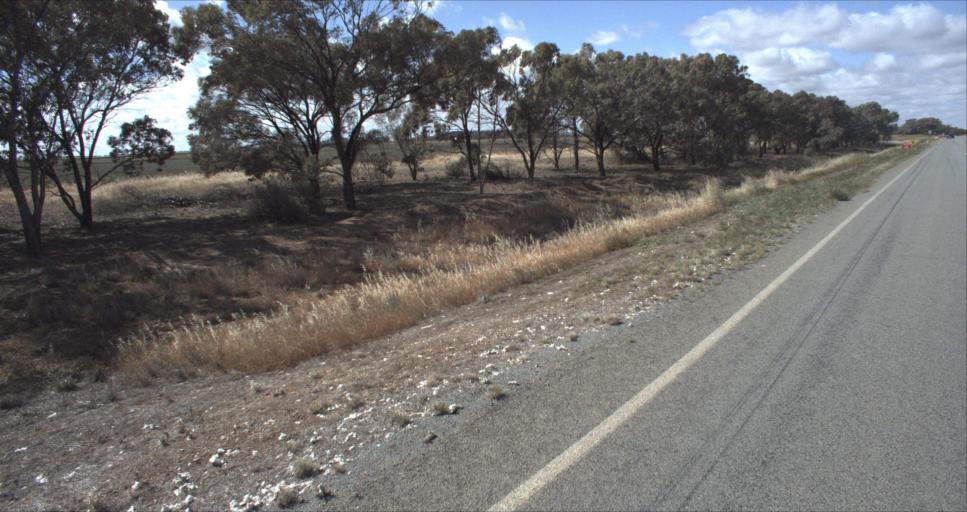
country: AU
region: New South Wales
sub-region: Murrumbidgee Shire
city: Darlington Point
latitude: -34.5501
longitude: 146.1708
